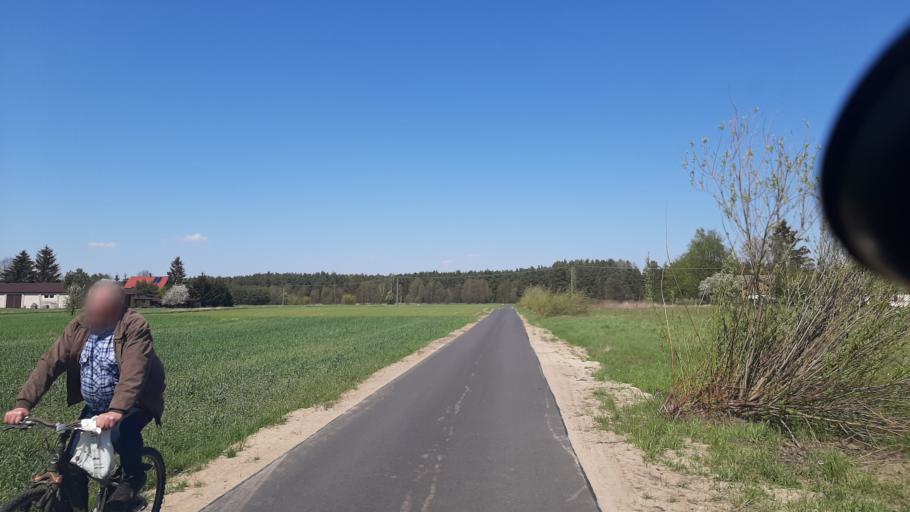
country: PL
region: Lublin Voivodeship
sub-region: Powiat lubelski
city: Garbow
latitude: 51.4043
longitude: 22.3225
